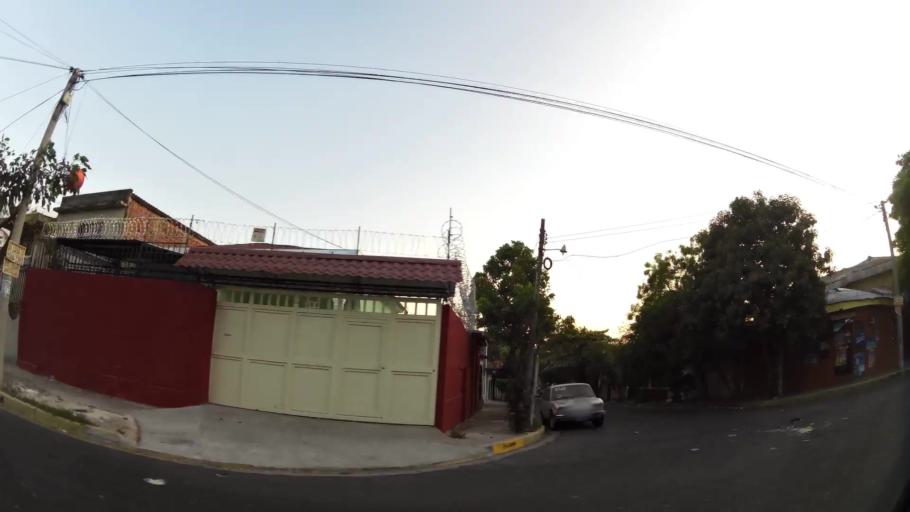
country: SV
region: San Salvador
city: Delgado
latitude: 13.7169
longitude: -89.1870
